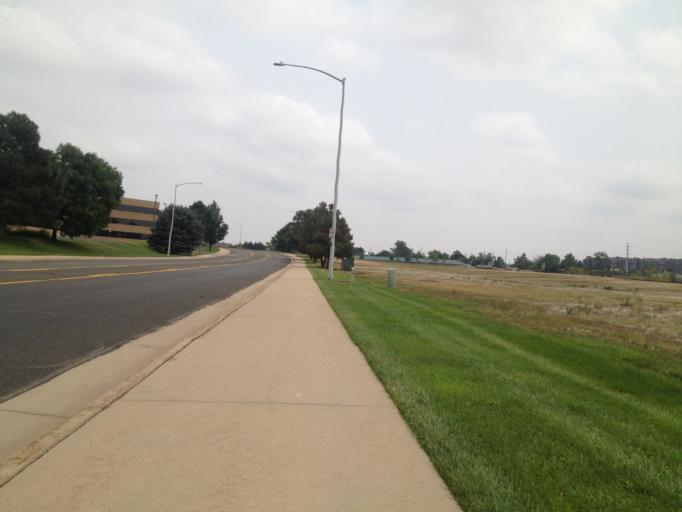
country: US
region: Colorado
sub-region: Broomfield County
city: Broomfield
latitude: 39.9256
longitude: -105.1065
